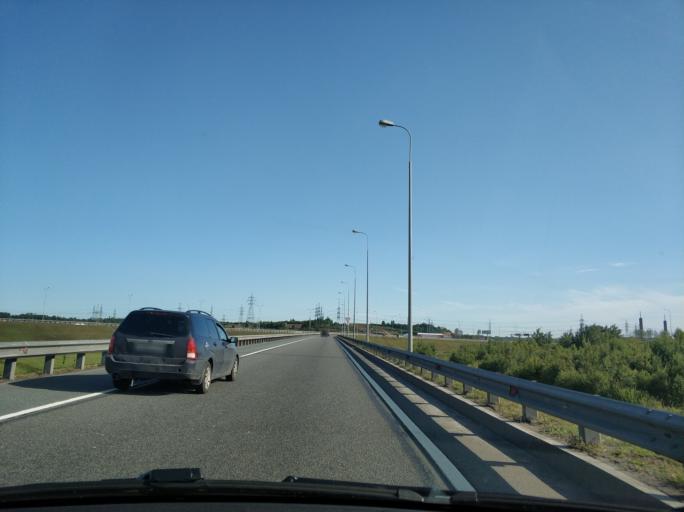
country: RU
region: Leningrad
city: Bugry
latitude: 60.0913
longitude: 30.3725
